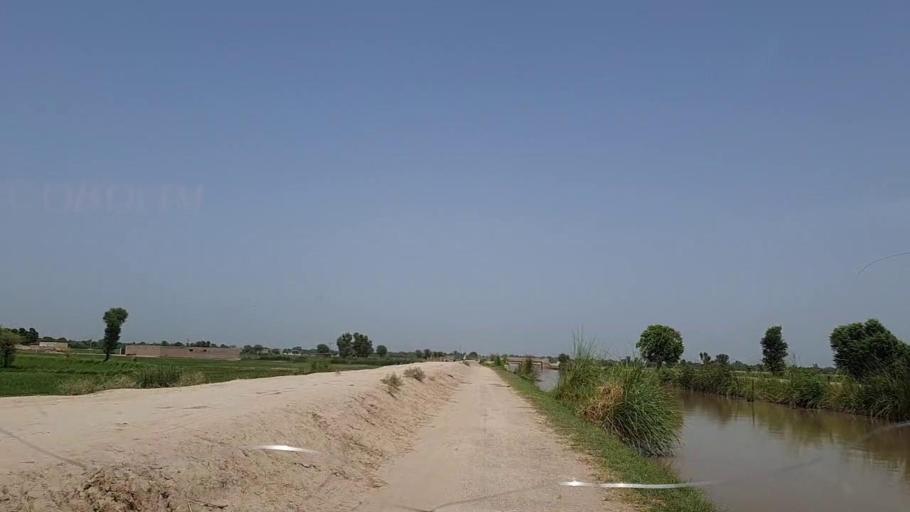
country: PK
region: Sindh
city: Tharu Shah
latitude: 26.9871
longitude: 68.0843
